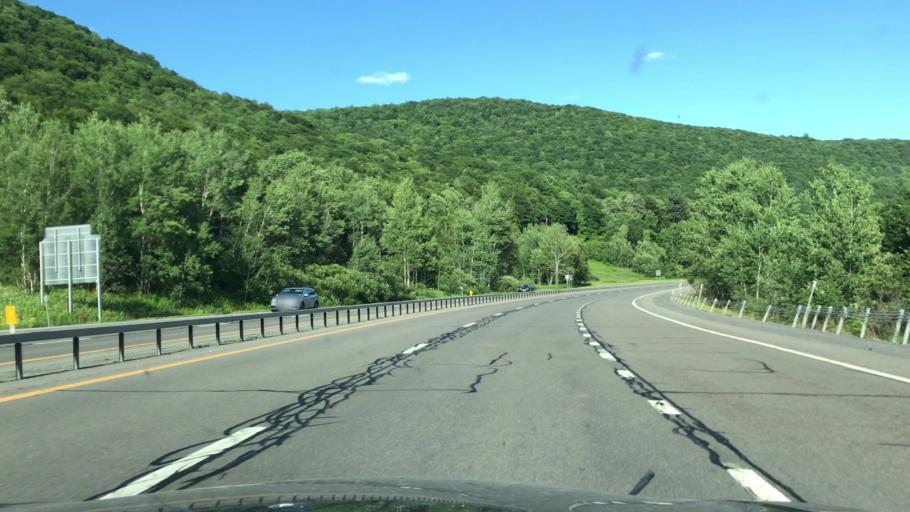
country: US
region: New York
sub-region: Delaware County
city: Hancock
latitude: 41.9664
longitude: -75.2565
